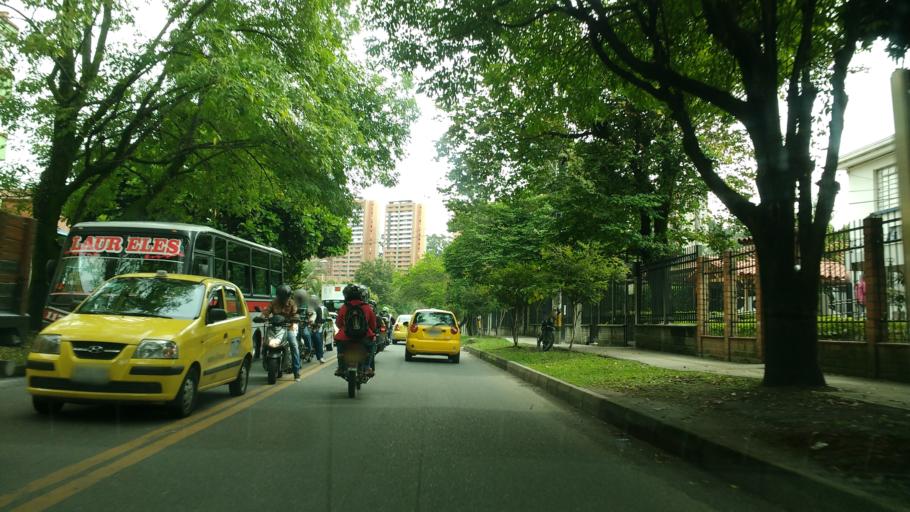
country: CO
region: Antioquia
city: Medellin
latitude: 6.2417
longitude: -75.6078
